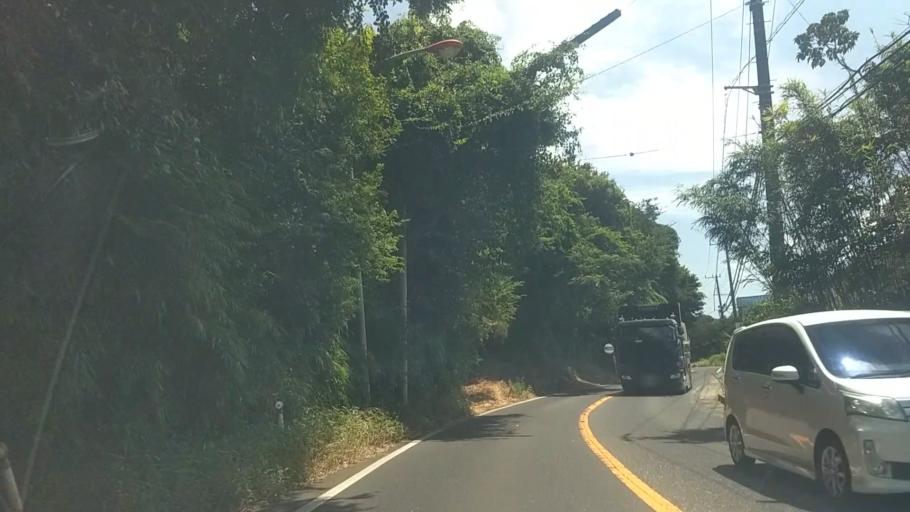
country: JP
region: Kanagawa
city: Miura
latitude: 35.2051
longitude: 139.6487
